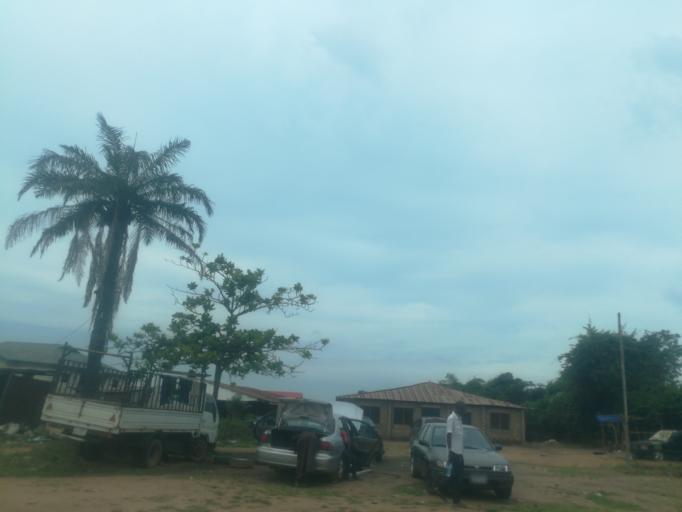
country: NG
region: Oyo
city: Ibadan
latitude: 7.3746
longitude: 3.9717
